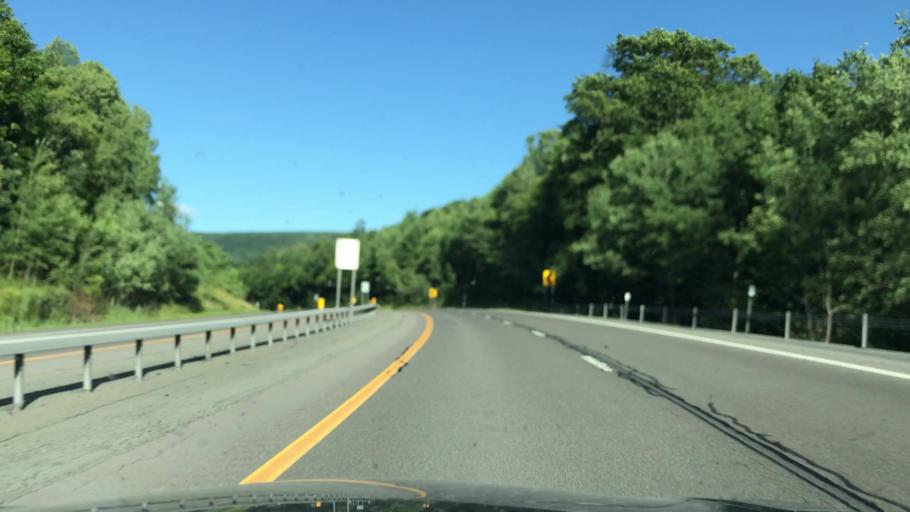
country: US
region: New York
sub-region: Delaware County
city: Hancock
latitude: 41.9692
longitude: -75.1860
